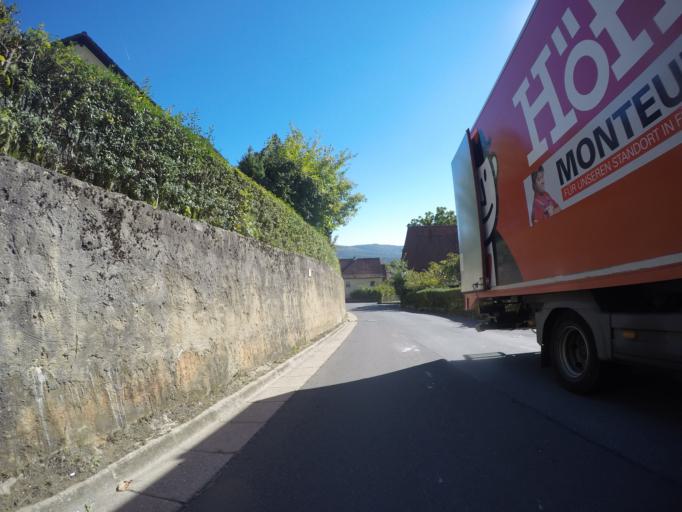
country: DE
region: Bavaria
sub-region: Upper Franconia
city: Weilersbach
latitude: 49.7575
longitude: 11.1384
